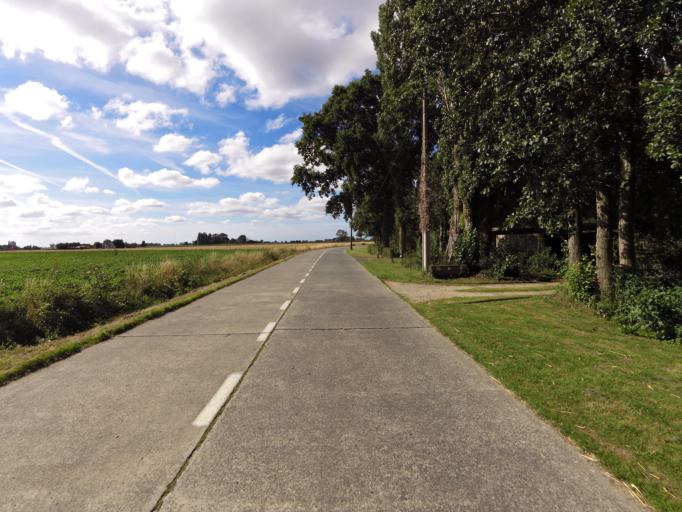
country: BE
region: Flanders
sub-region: Provincie West-Vlaanderen
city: Alveringem
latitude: 50.9761
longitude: 2.6615
